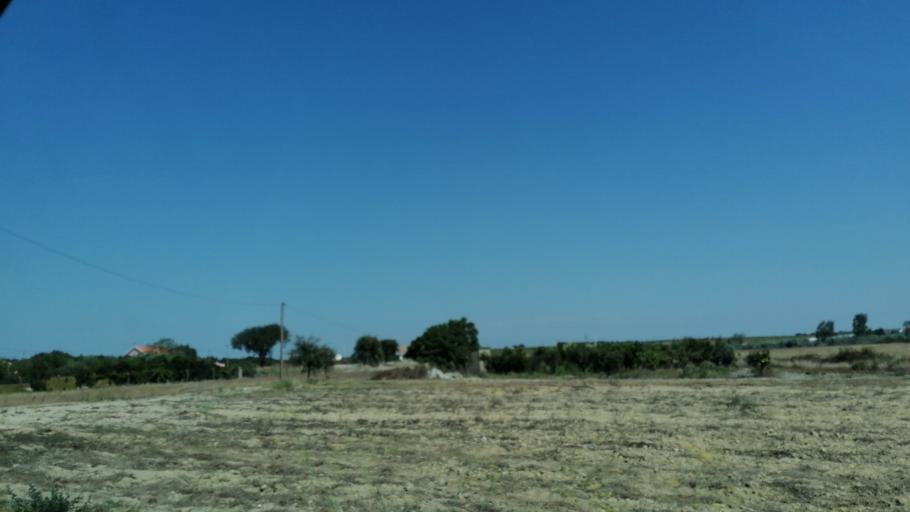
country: PT
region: Santarem
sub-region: Benavente
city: Poceirao
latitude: 38.7041
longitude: -8.7211
